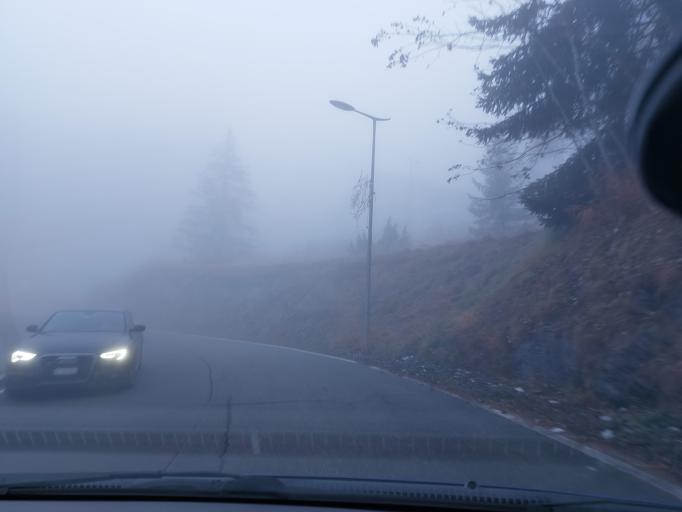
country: CH
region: Valais
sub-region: Sierre District
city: Lens
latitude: 46.3053
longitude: 7.4536
